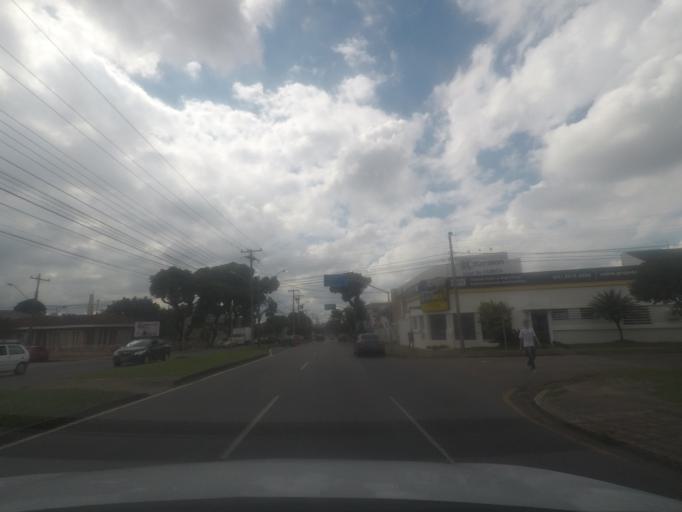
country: BR
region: Parana
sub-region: Curitiba
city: Curitiba
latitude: -25.4530
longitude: -49.2647
